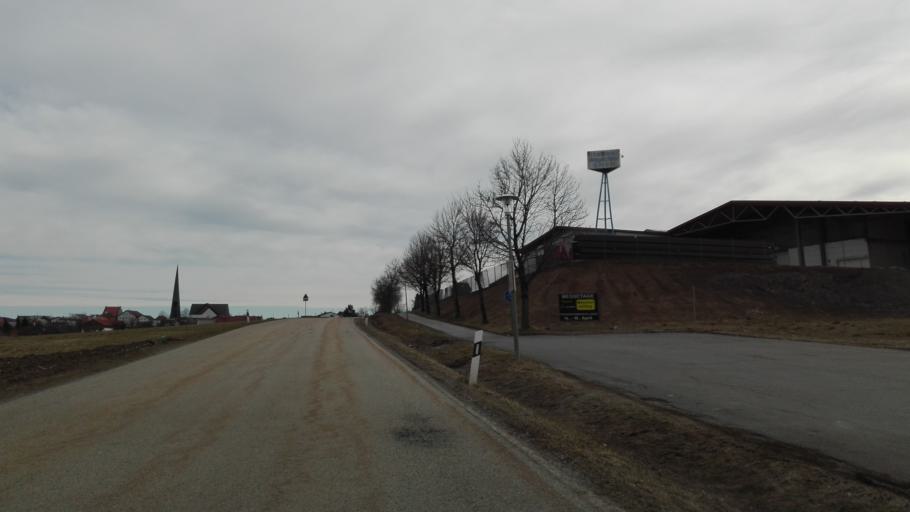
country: DE
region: Bavaria
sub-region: Lower Bavaria
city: Wegscheid
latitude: 48.6075
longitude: 13.7838
